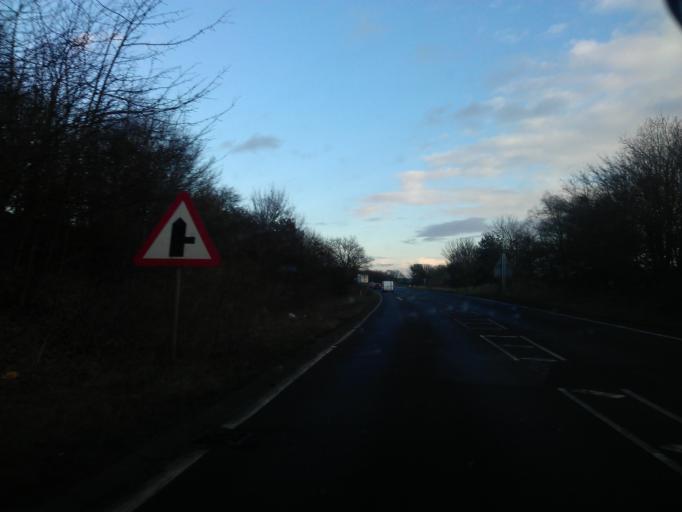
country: GB
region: England
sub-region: Essex
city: Mistley
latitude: 51.9139
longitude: 1.1555
